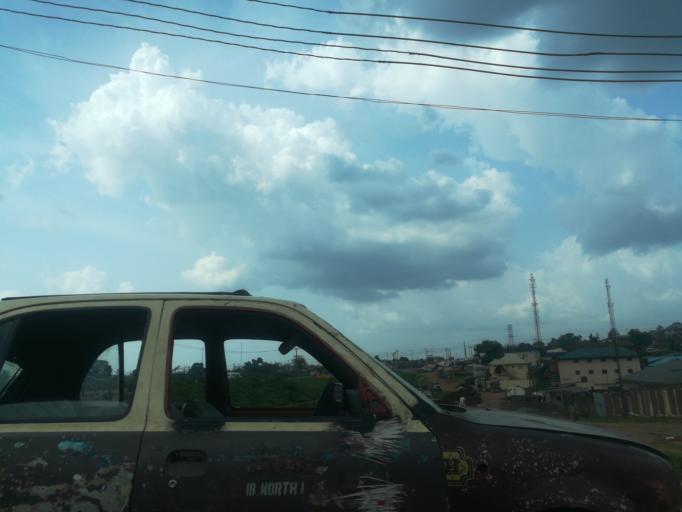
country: NG
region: Oyo
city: Moniya
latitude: 7.4739
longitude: 3.9151
